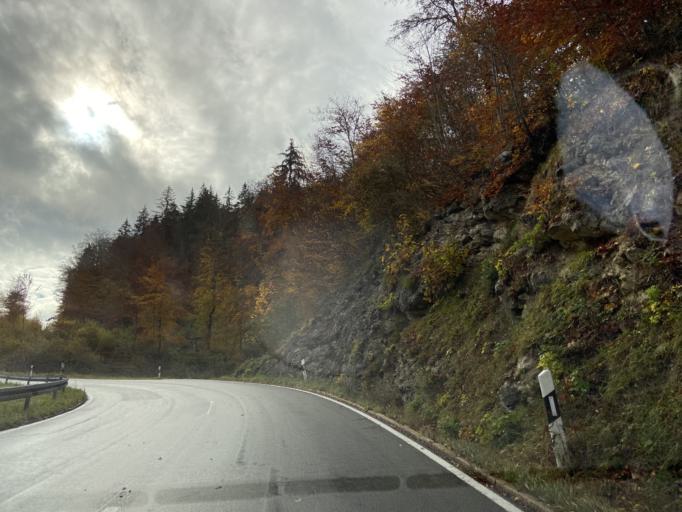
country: DE
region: Baden-Wuerttemberg
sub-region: Tuebingen Region
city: Beuron
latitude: 48.0524
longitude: 8.9630
